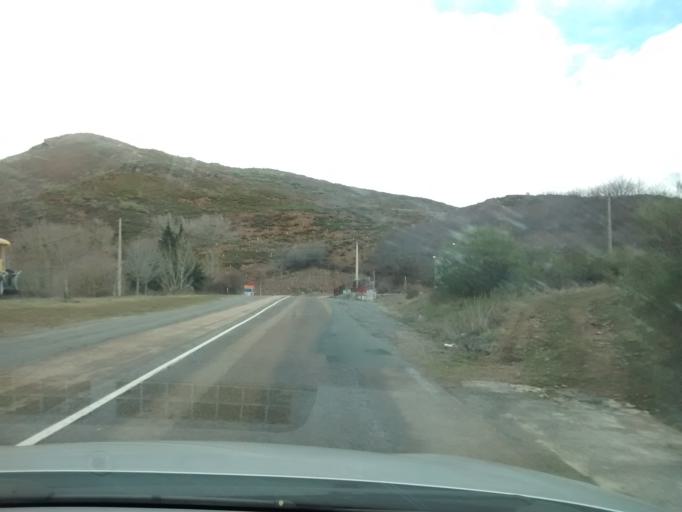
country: ES
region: Castille and Leon
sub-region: Provincia de Burgos
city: Espinosa de los Monteros
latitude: 43.0861
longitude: -3.5570
